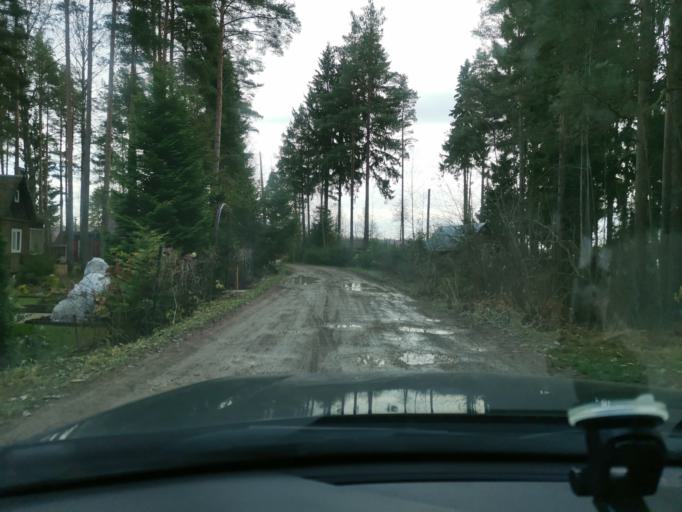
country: EE
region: Ida-Virumaa
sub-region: Sillamaee linn
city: Sillamae
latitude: 59.2540
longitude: 27.9136
